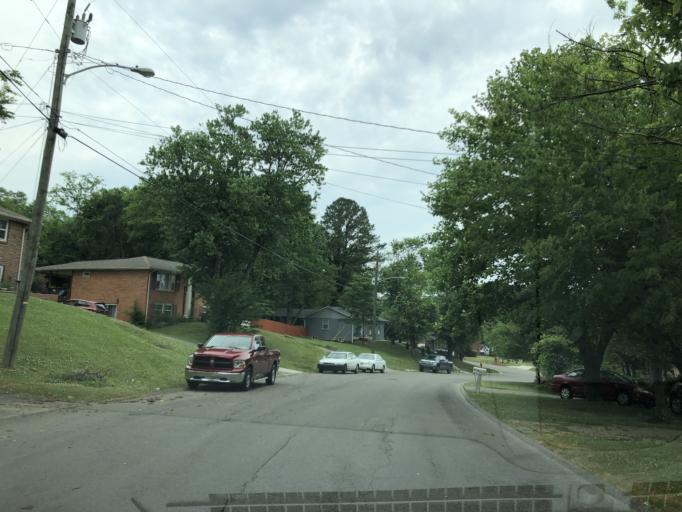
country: US
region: Tennessee
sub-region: Davidson County
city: Oak Hill
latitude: 36.0779
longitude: -86.6845
